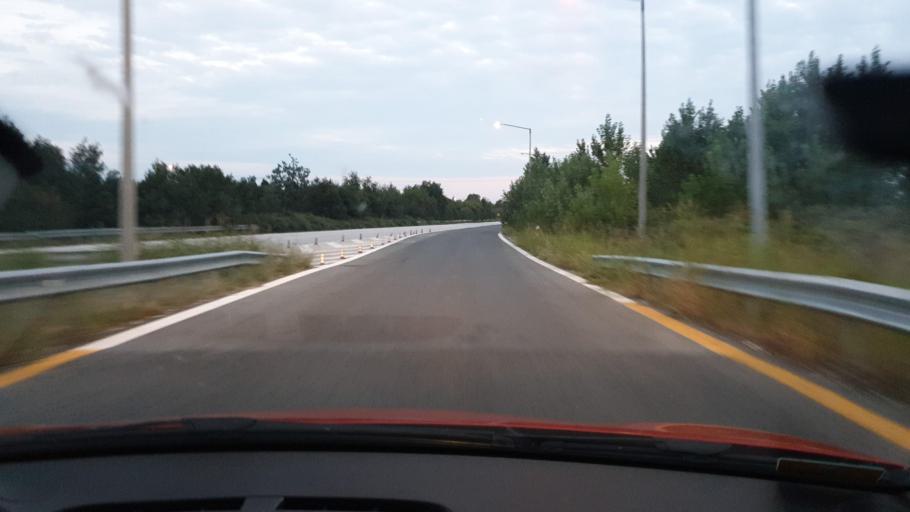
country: GR
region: Central Macedonia
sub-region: Nomos Kilkis
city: Polykastro
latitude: 40.9885
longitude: 22.6040
